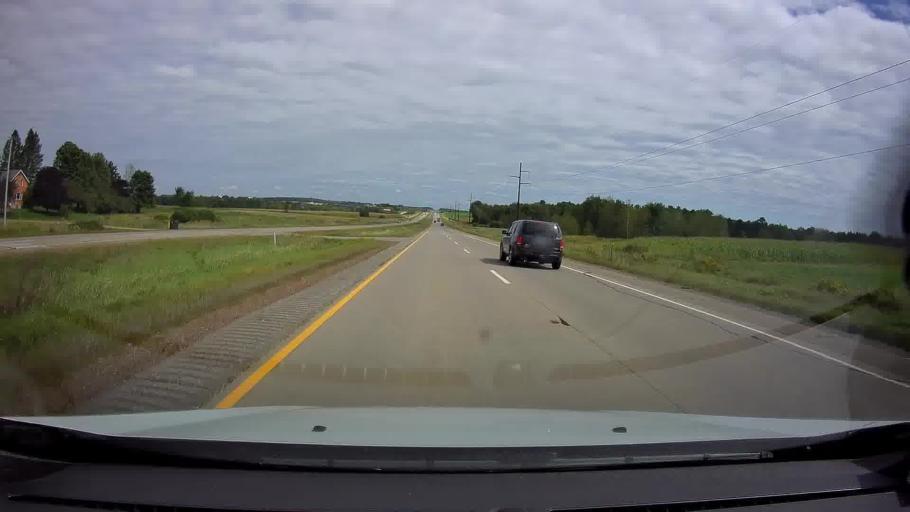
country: US
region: Wisconsin
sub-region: Marathon County
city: Marathon
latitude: 44.9441
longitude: -89.8926
